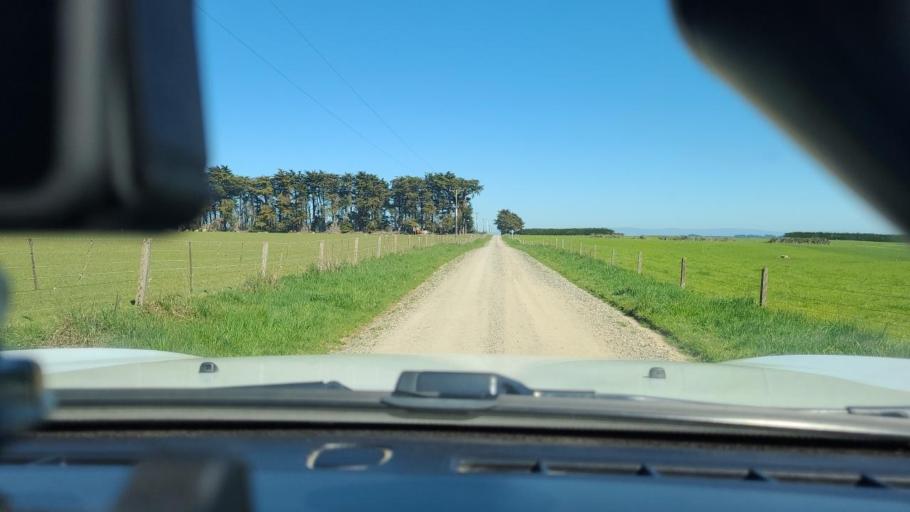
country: NZ
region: Southland
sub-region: Invercargill City
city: Invercargill
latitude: -46.3147
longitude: 168.4532
